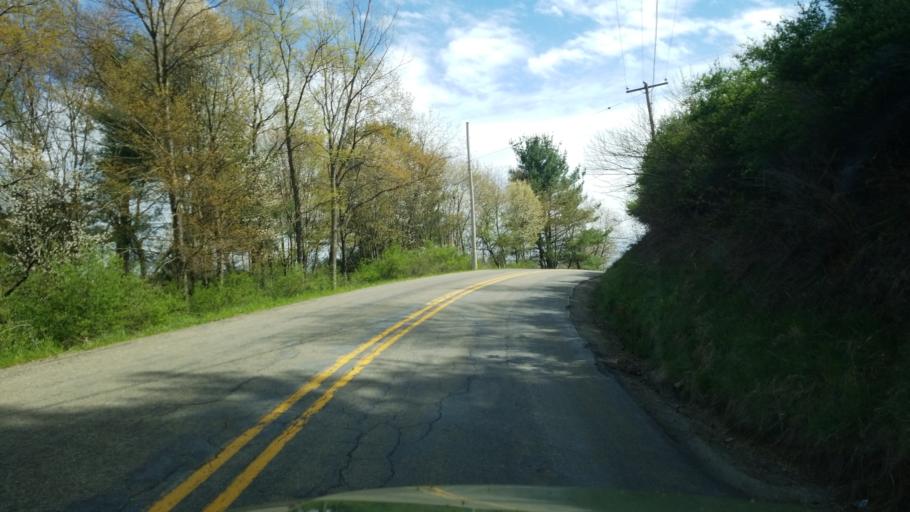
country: US
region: Pennsylvania
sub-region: Jefferson County
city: Brockway
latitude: 41.2305
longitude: -78.8508
